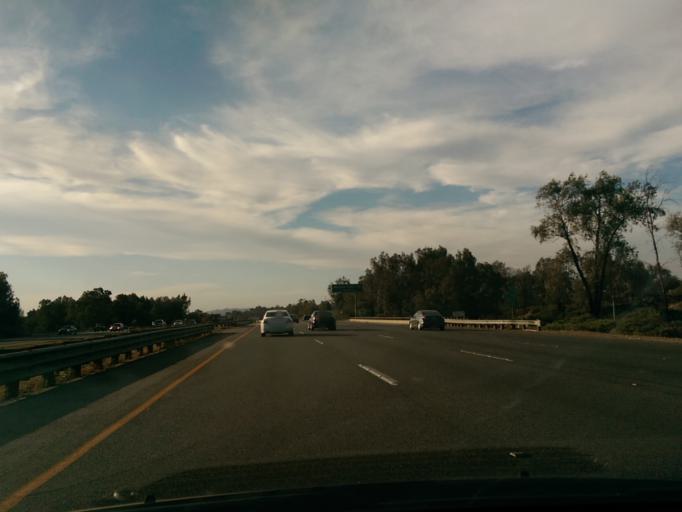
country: US
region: California
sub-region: Riverside County
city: Temecula
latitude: 33.4794
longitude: -117.1402
